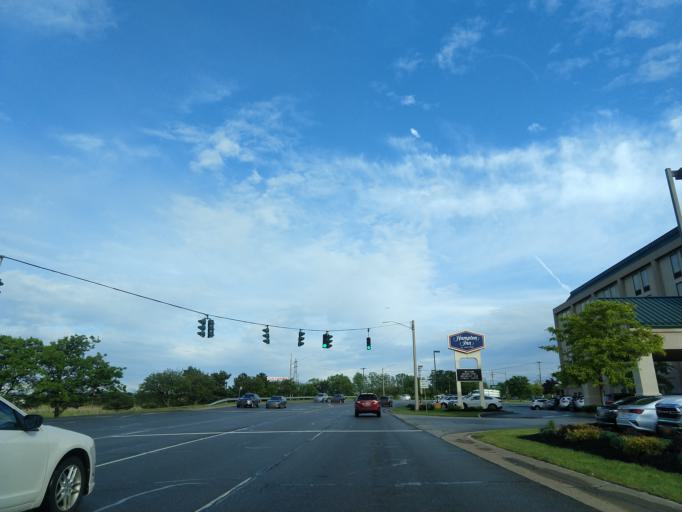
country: US
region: New York
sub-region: Erie County
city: West Seneca
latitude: 42.8304
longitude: -78.7889
